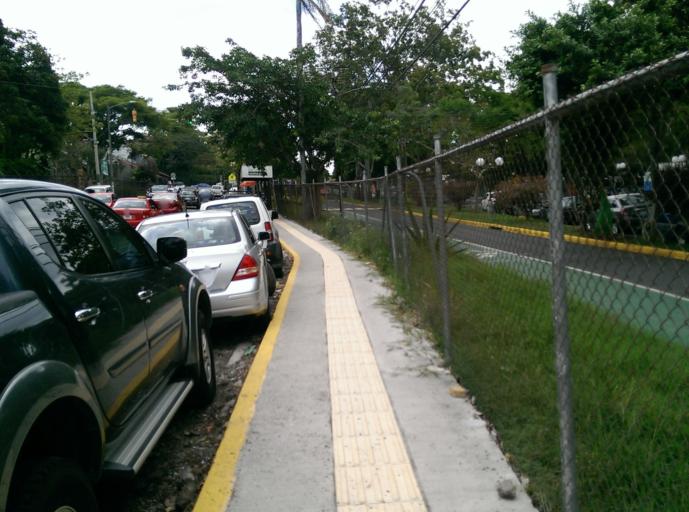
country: CR
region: San Jose
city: San Pedro
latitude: 9.9389
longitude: -84.0492
